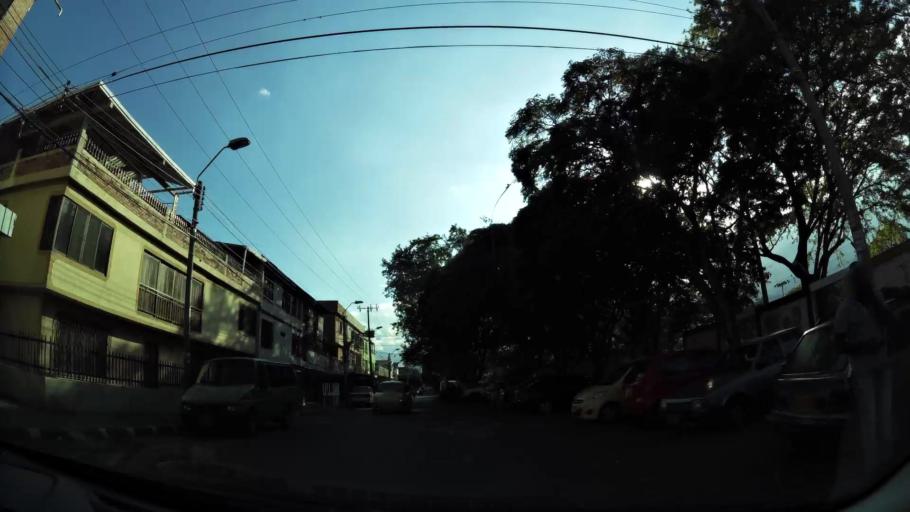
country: CO
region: Valle del Cauca
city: Cali
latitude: 3.4035
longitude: -76.5053
